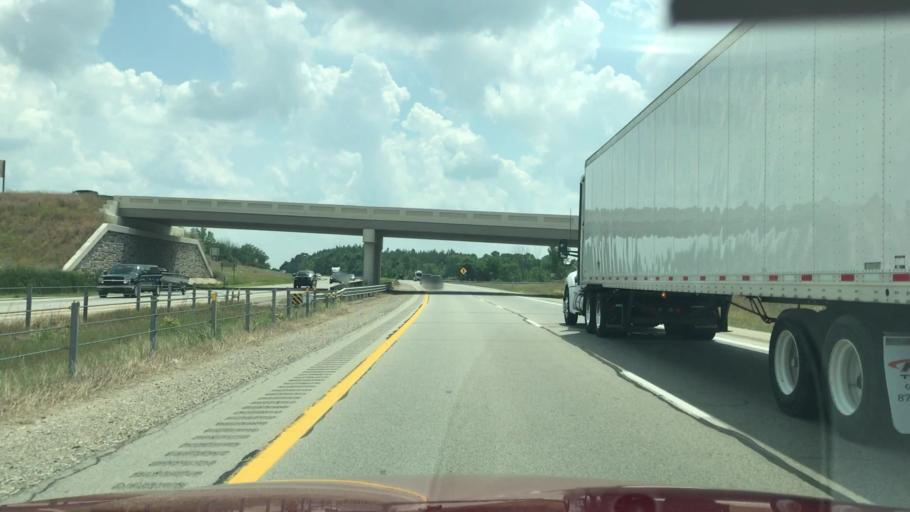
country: US
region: Michigan
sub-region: Allegan County
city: Wayland
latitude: 42.7254
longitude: -85.6726
